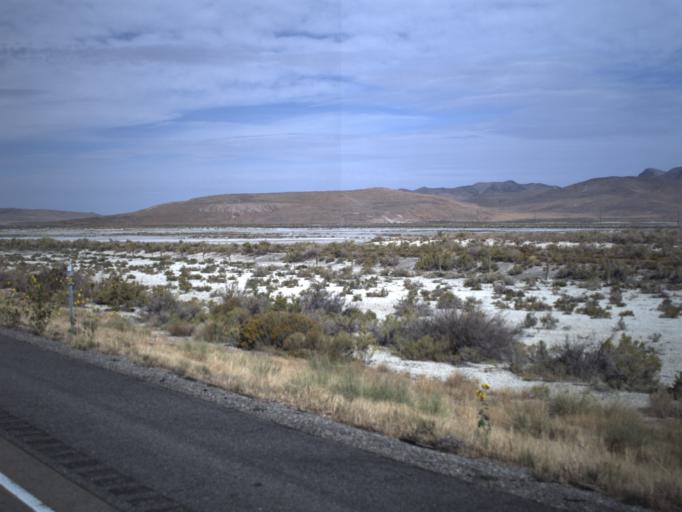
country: US
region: Utah
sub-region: Tooele County
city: Grantsville
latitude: 40.7555
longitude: -112.7463
